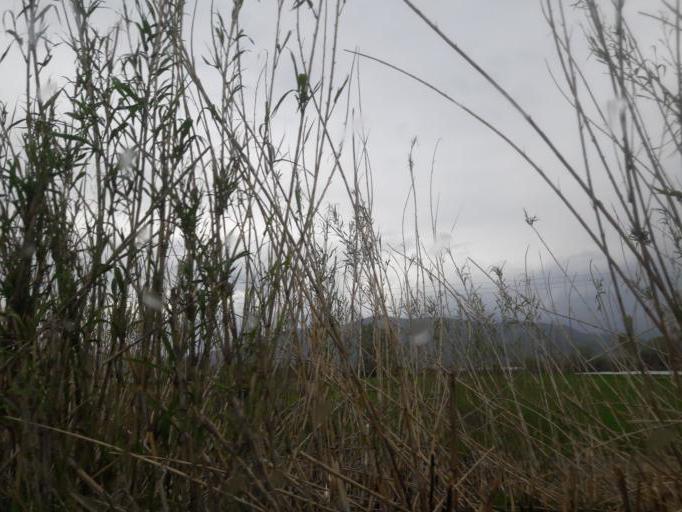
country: AL
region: Shkoder
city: Vukatane
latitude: 42.0001
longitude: 19.5426
